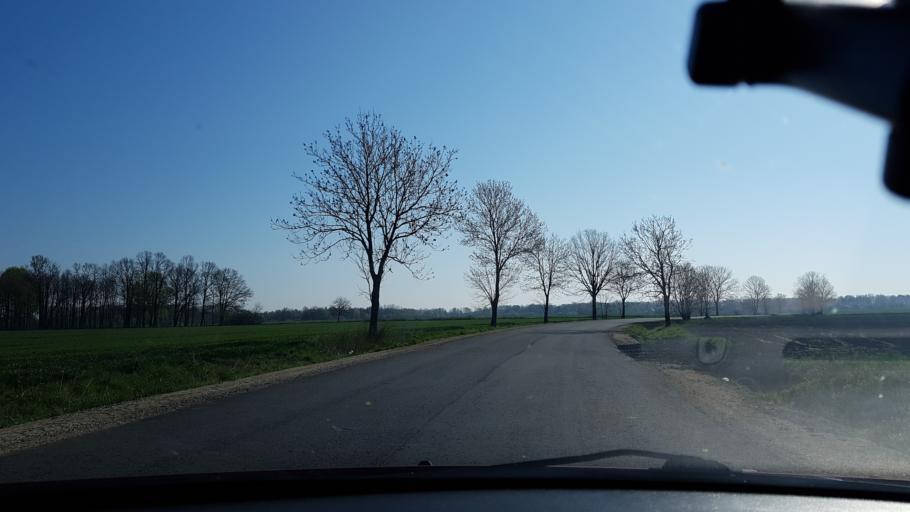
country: CZ
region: Olomoucky
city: Vidnava
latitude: 50.4265
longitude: 17.2407
